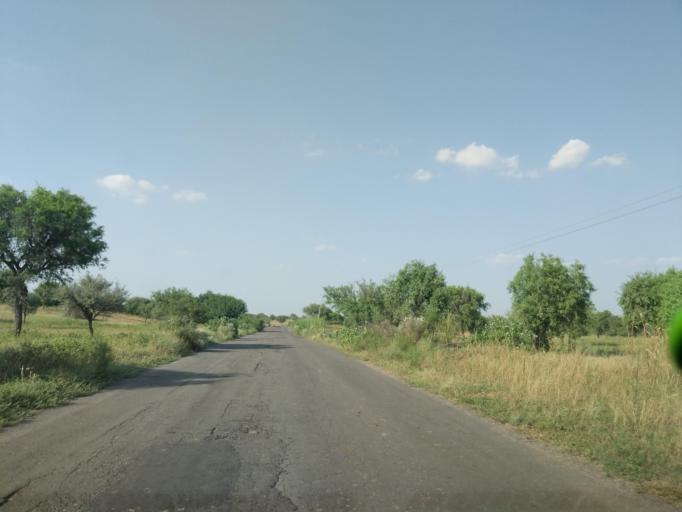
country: IN
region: Rajasthan
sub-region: Churu
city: Rajgarh
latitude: 28.4836
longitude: 75.3690
